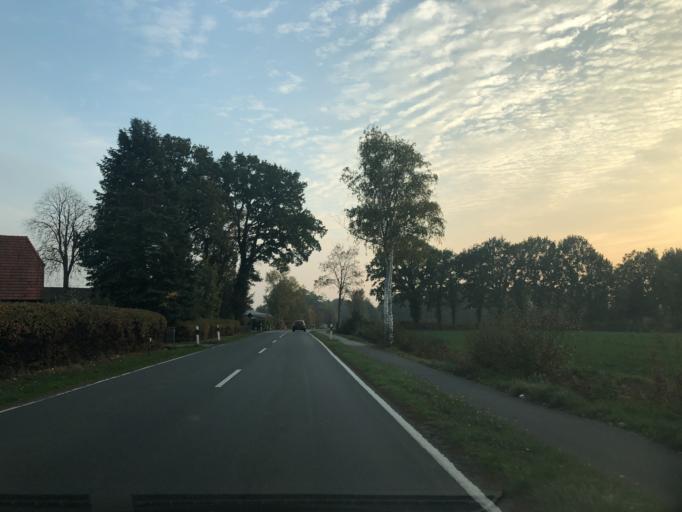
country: DE
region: Lower Saxony
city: Wardenburg
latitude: 53.0617
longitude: 8.1615
